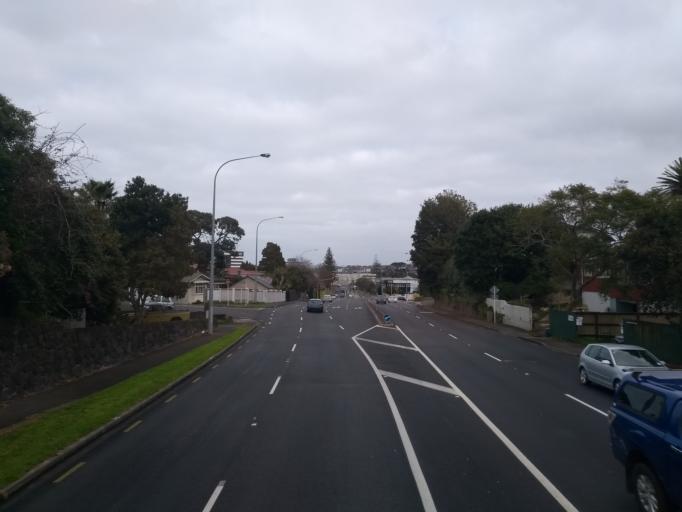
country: NZ
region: Auckland
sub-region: Auckland
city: Tamaki
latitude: -36.8993
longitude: 174.8177
